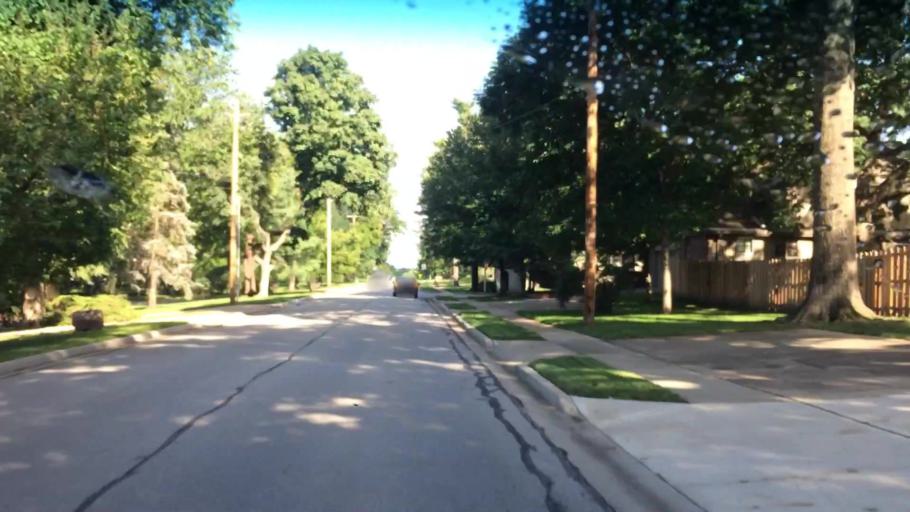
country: US
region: Kansas
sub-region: Johnson County
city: Prairie Village
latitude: 38.9713
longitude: -94.6459
